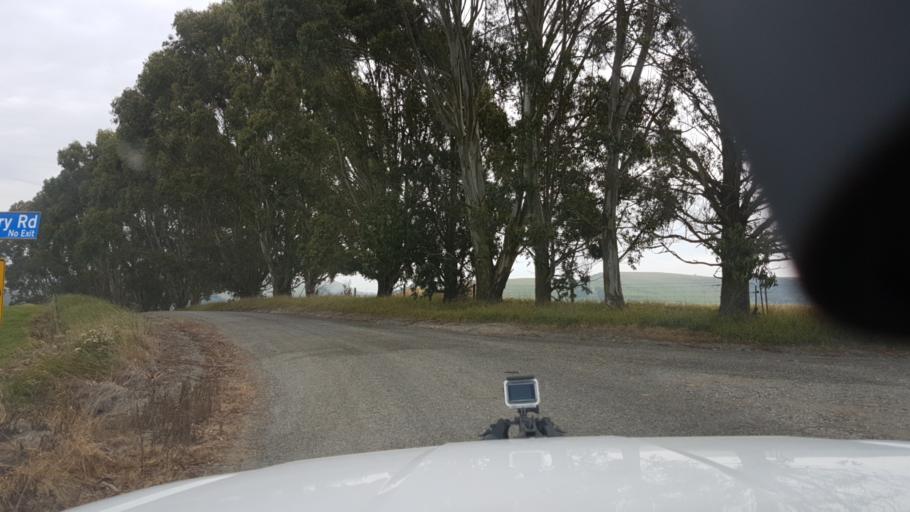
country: NZ
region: Otago
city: Oamaru
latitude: -45.0331
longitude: 170.9656
